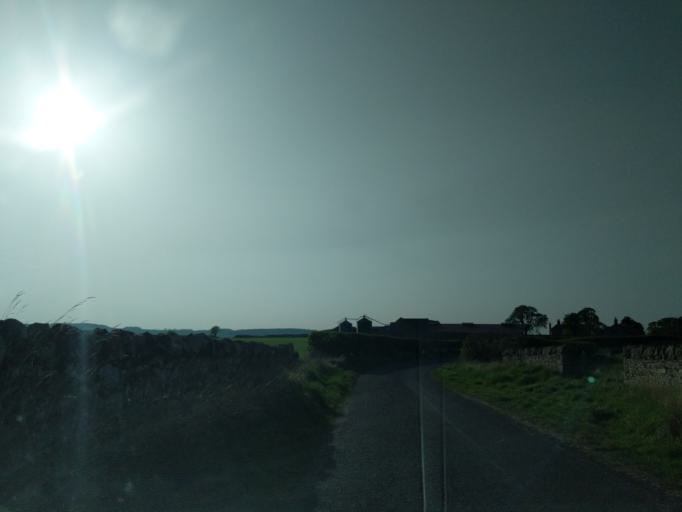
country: GB
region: Scotland
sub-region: Fife
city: Pathhead
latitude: 55.8678
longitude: -2.9553
